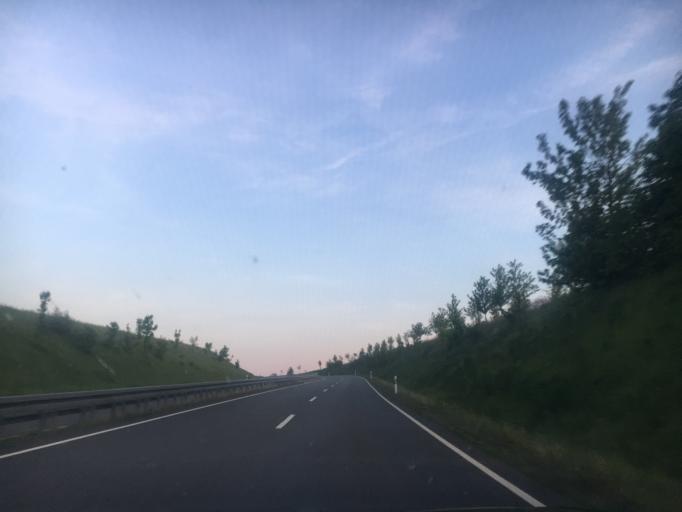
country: DE
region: Thuringia
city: Gera
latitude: 50.8857
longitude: 12.1136
